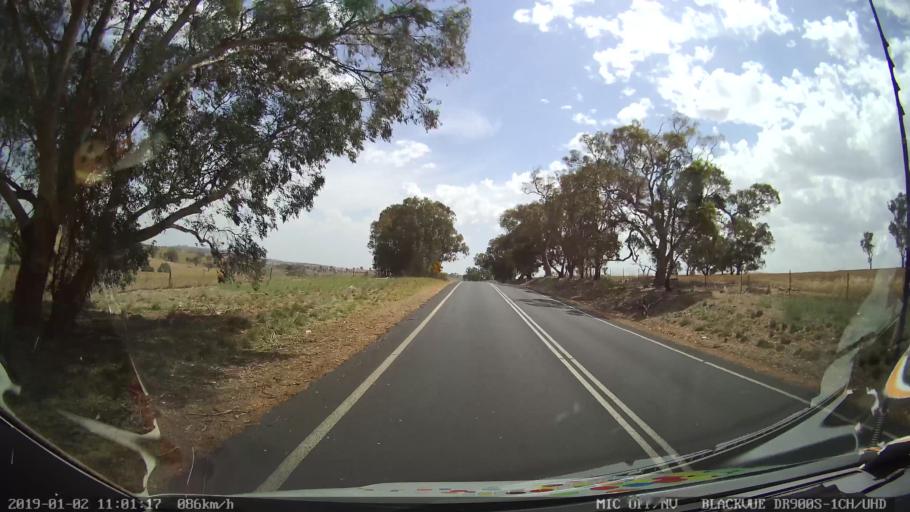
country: AU
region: New South Wales
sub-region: Young
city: Young
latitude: -34.5996
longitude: 148.3188
